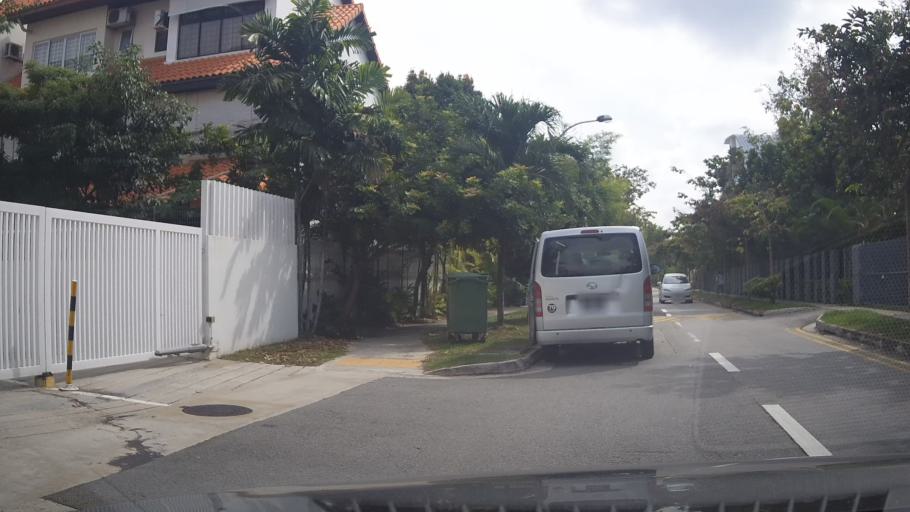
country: SG
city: Singapore
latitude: 1.3113
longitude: 103.9141
